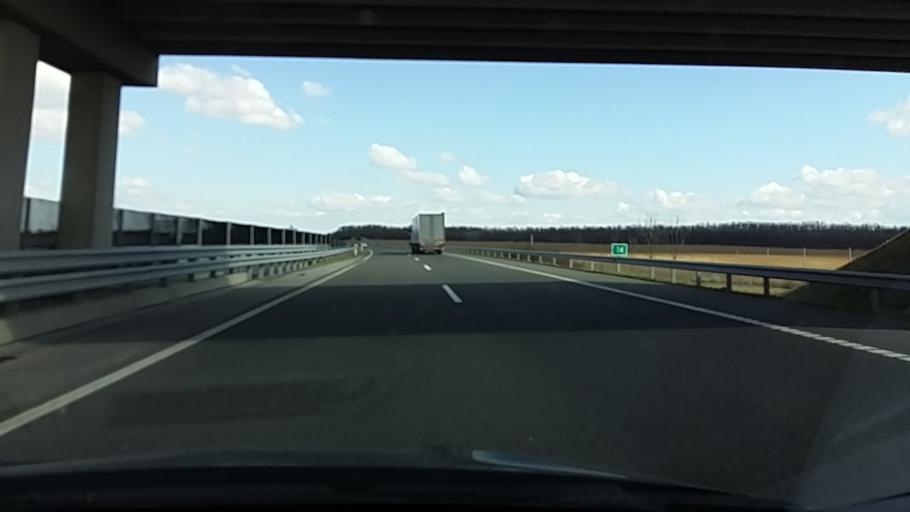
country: HU
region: Baranya
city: Kozarmisleny
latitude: 46.0196
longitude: 18.3023
